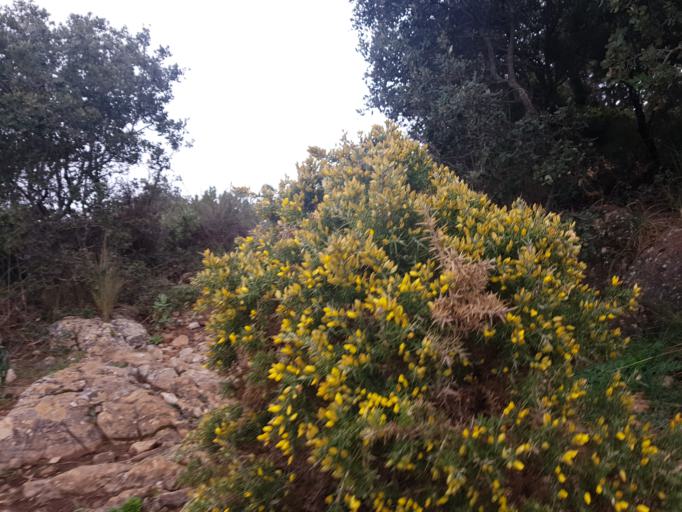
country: ES
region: Andalusia
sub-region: Provincia de Malaga
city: Ojen
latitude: 36.5646
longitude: -4.8978
